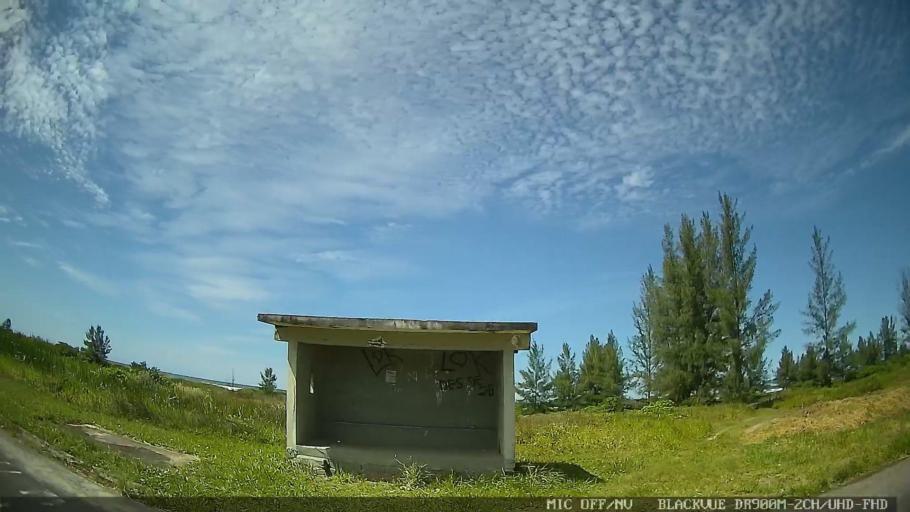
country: BR
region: Sao Paulo
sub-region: Iguape
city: Iguape
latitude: -24.8085
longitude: -47.6396
